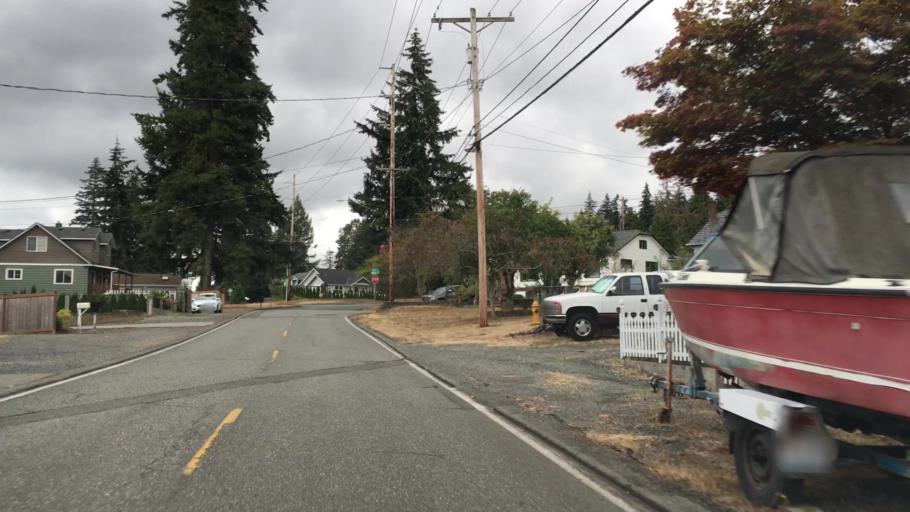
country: US
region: Washington
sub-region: Snohomish County
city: Everett
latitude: 47.9444
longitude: -122.2048
